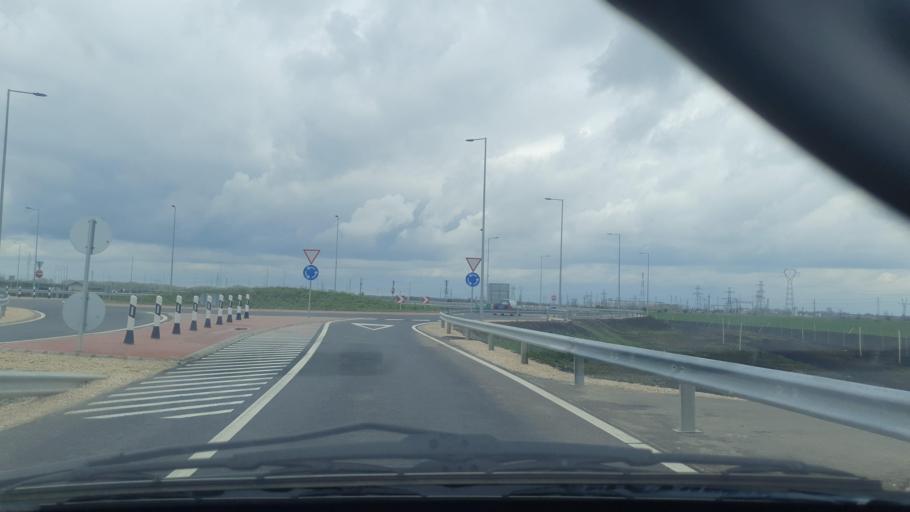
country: HU
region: Jasz-Nagykun-Szolnok
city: Zagyvarekas
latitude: 47.2112
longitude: 20.1327
